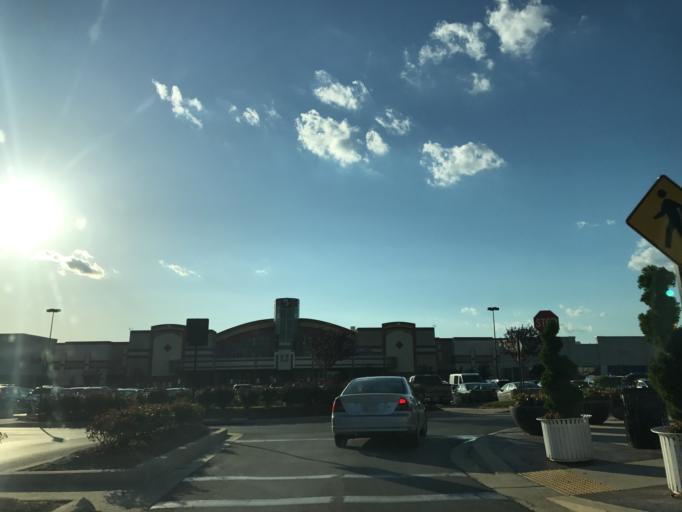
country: US
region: Maryland
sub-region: Anne Arundel County
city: Crofton
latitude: 39.0333
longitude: -76.6865
